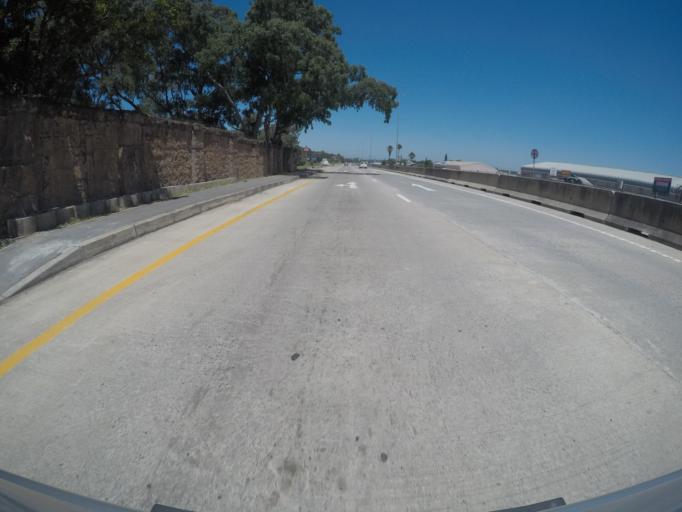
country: ZA
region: Eastern Cape
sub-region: Buffalo City Metropolitan Municipality
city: East London
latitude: -32.9405
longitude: 27.9747
